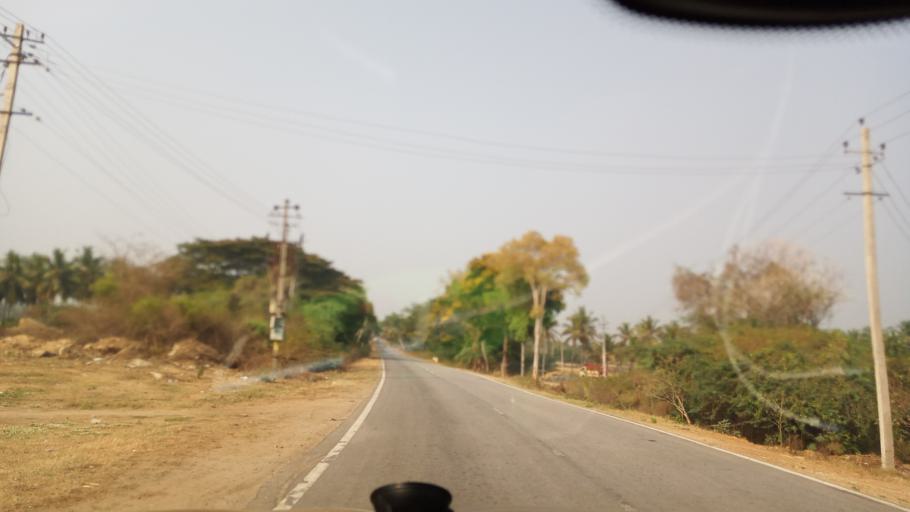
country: IN
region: Karnataka
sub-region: Mandya
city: Belluru
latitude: 12.9595
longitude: 76.7588
